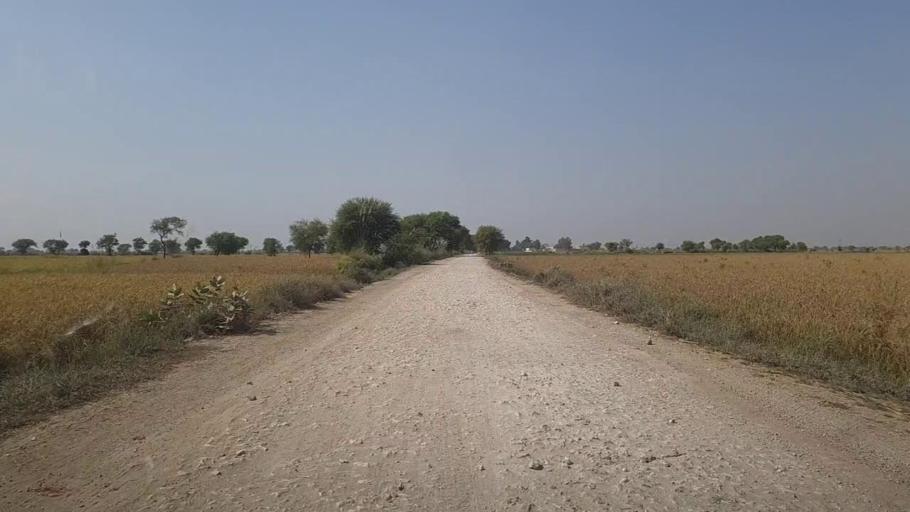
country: PK
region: Sindh
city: Kandhkot
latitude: 28.3938
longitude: 69.2996
